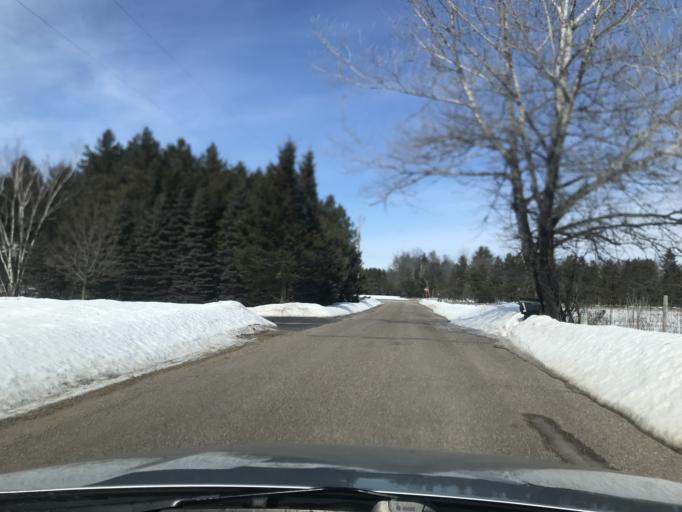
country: US
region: Wisconsin
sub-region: Marinette County
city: Peshtigo
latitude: 45.2265
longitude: -87.9627
